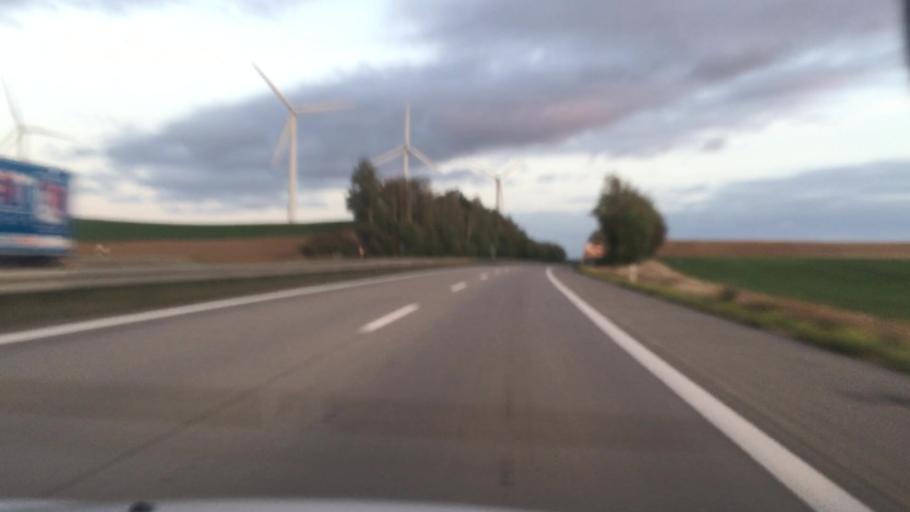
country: DE
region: Saxony
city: Mochau
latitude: 51.1317
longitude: 13.1630
